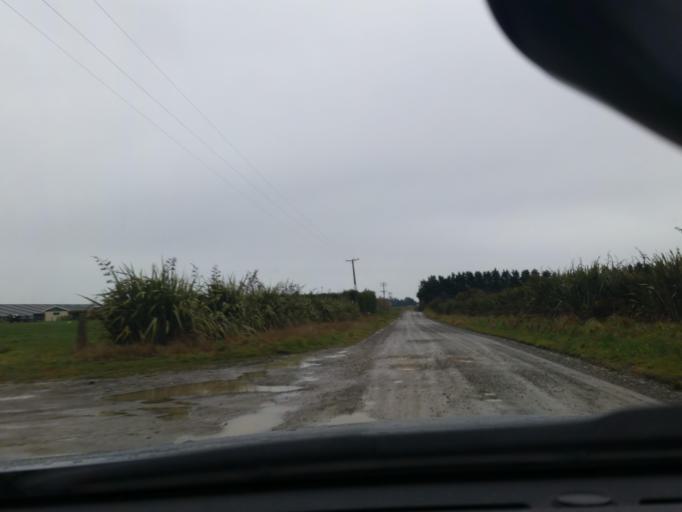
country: NZ
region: Southland
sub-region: Southland District
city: Winton
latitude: -46.2486
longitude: 168.4657
